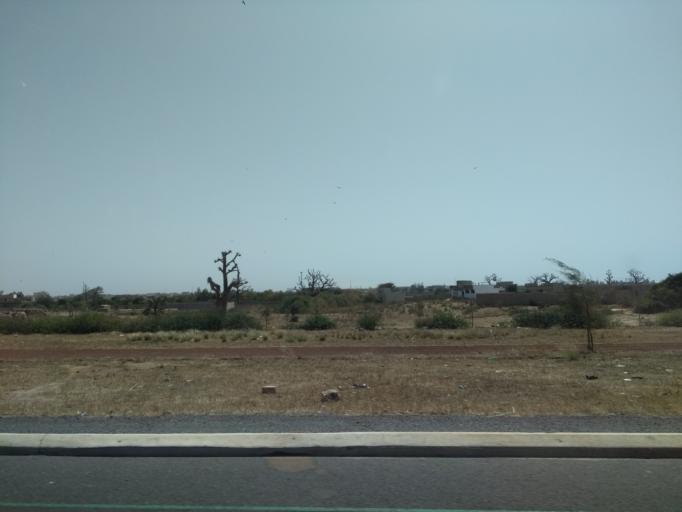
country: SN
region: Thies
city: Thies
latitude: 14.7375
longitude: -17.1811
